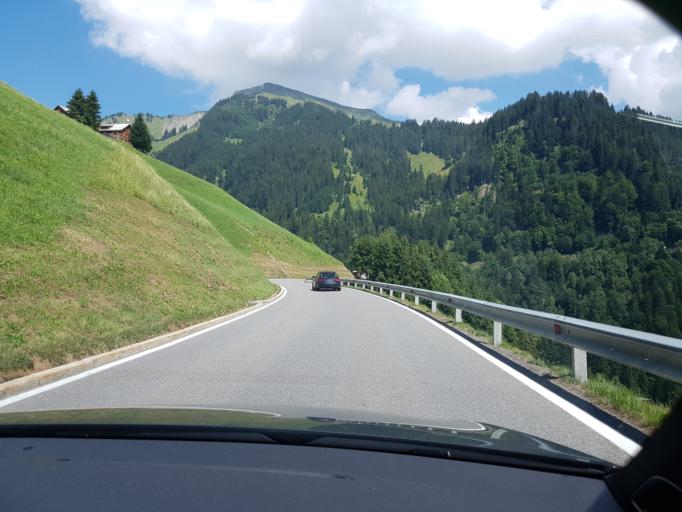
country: AT
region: Vorarlberg
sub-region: Politischer Bezirk Bregenz
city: Damuels
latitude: 47.2489
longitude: 9.9128
